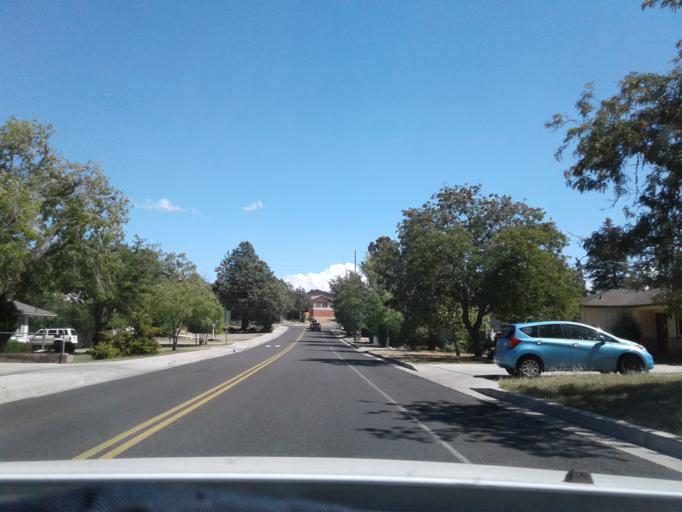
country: US
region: Arizona
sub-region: Yavapai County
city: Prescott
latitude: 34.5708
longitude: -112.4752
